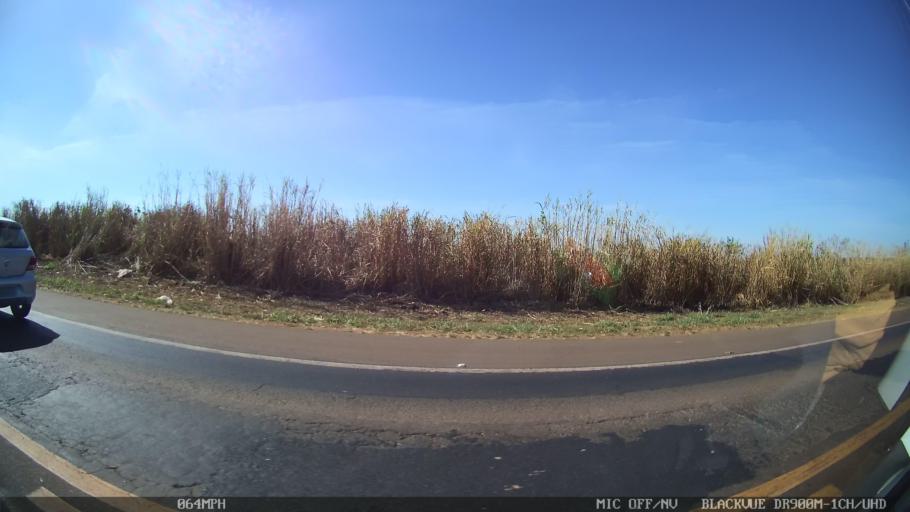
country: BR
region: Sao Paulo
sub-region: Olimpia
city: Olimpia
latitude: -20.7125
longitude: -48.8777
